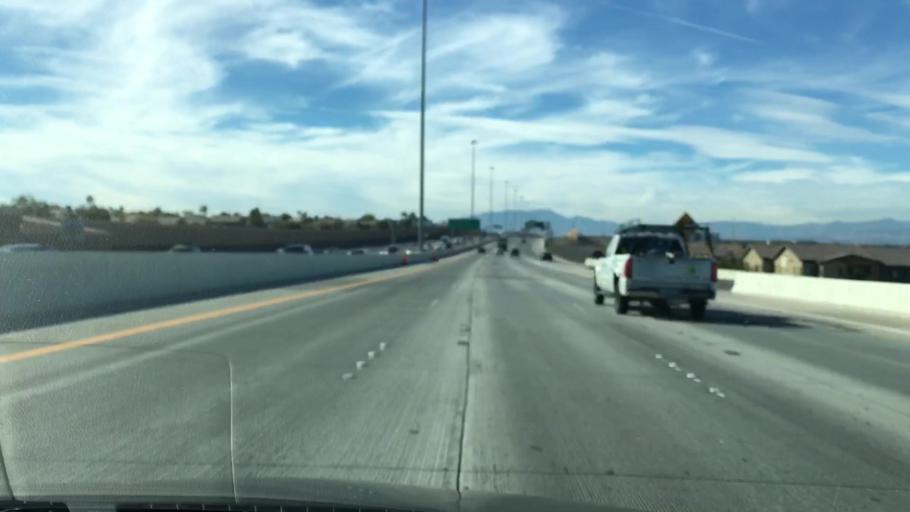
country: US
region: Nevada
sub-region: Clark County
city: Henderson
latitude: 36.0316
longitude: -115.0320
